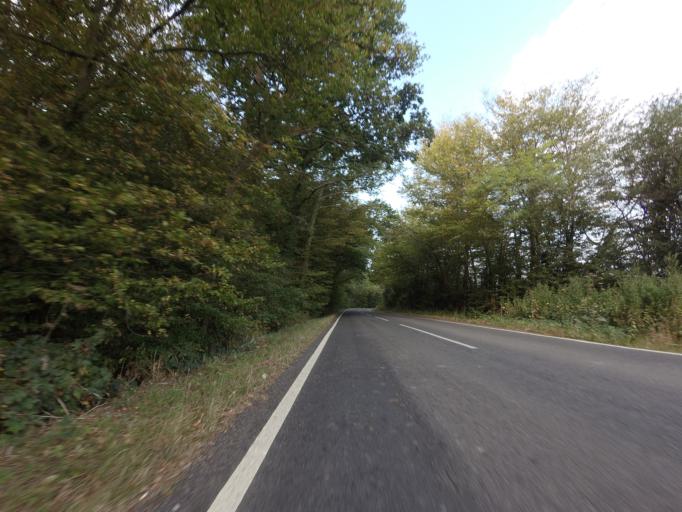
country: GB
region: England
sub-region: Kent
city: Tenterden
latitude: 51.1259
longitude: 0.7320
